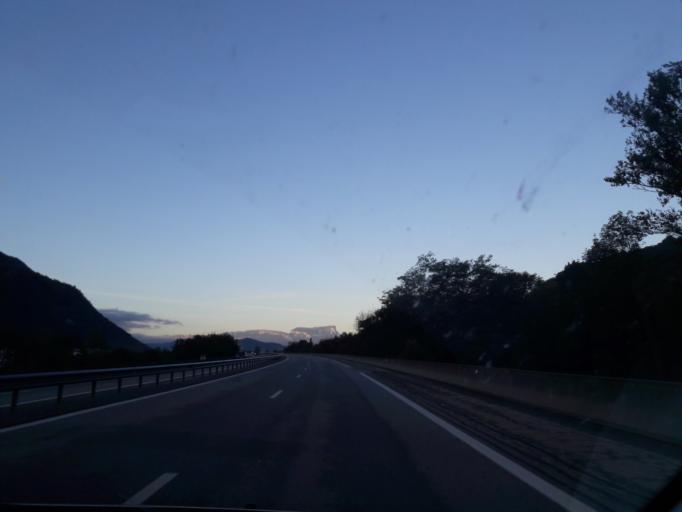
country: FR
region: Rhone-Alpes
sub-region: Departement de la Savoie
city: Aiton
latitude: 45.5586
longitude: 6.2620
